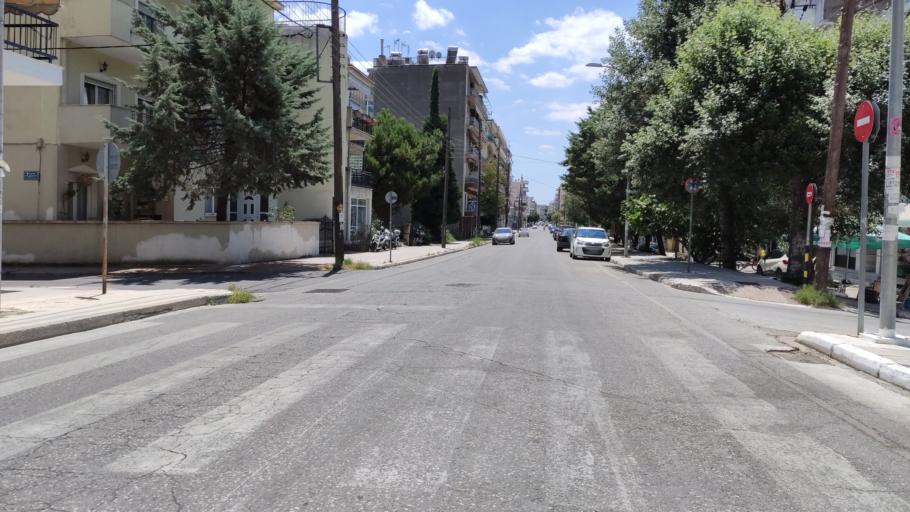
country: GR
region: East Macedonia and Thrace
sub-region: Nomos Rodopis
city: Komotini
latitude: 41.1268
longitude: 25.4115
